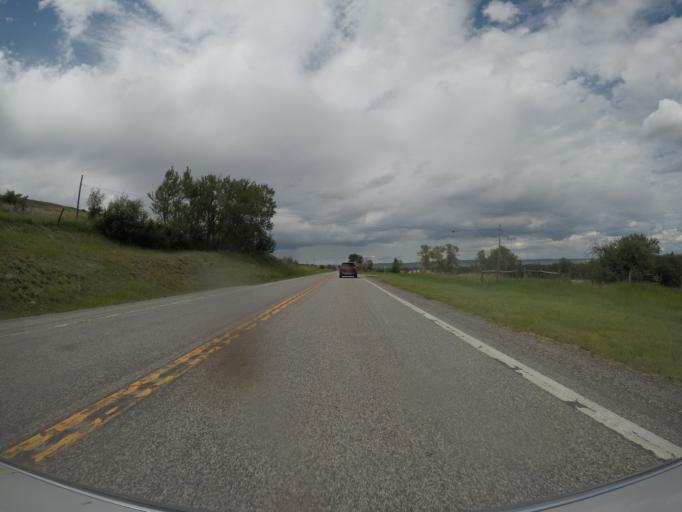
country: US
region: Montana
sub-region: Sweet Grass County
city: Big Timber
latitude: 45.8142
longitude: -109.9581
